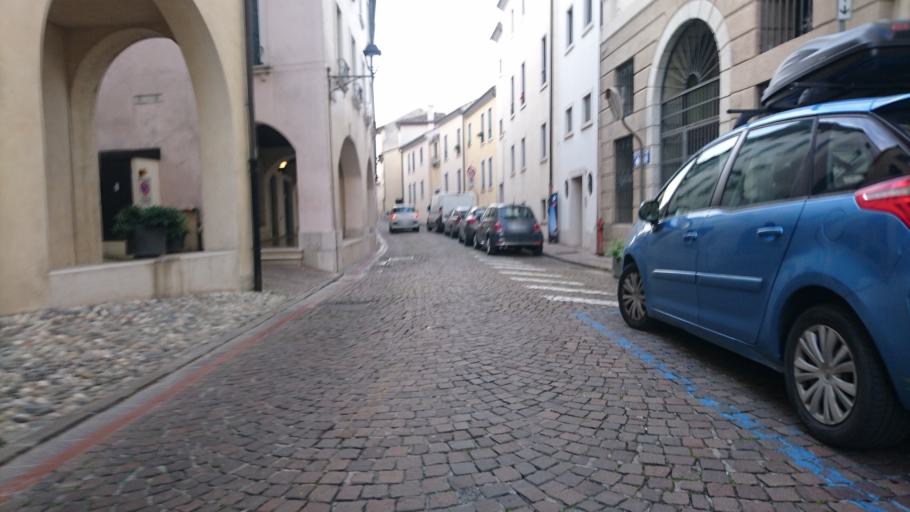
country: IT
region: Veneto
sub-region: Provincia di Treviso
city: Conegliano
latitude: 45.8881
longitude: 12.2994
